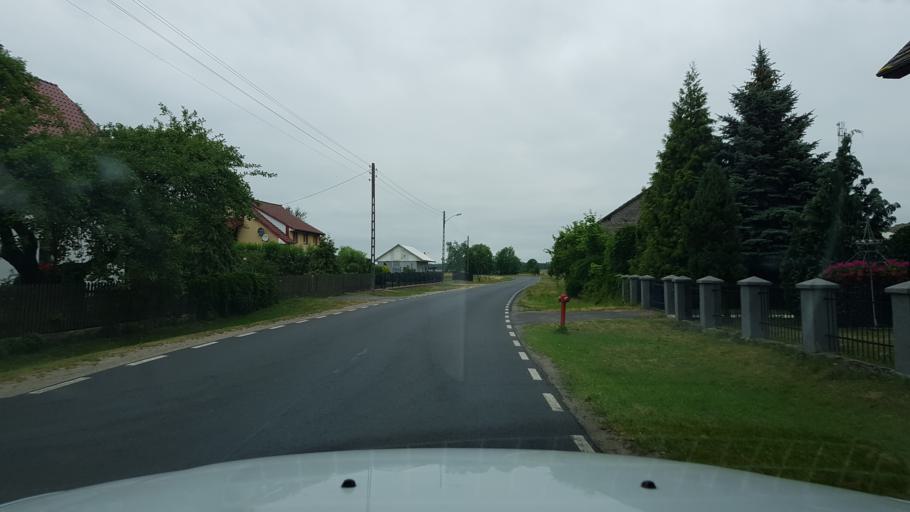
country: PL
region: West Pomeranian Voivodeship
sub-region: Powiat gryficki
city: Brojce
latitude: 53.9396
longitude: 15.4052
